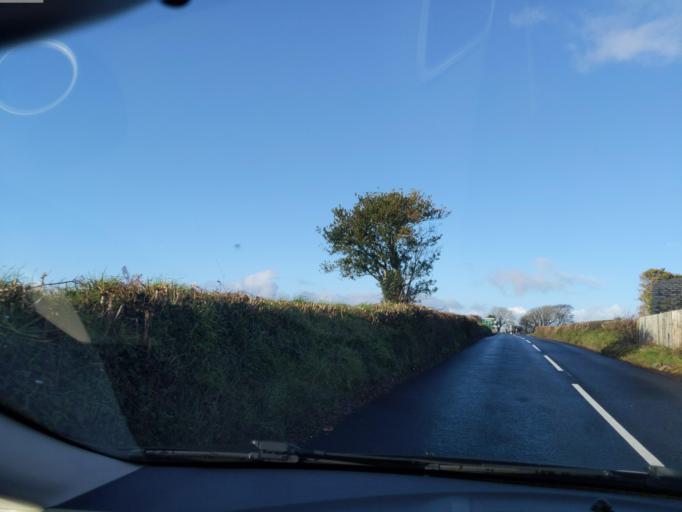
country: GB
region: England
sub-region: Devon
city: Okehampton
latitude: 50.7491
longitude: -4.0242
